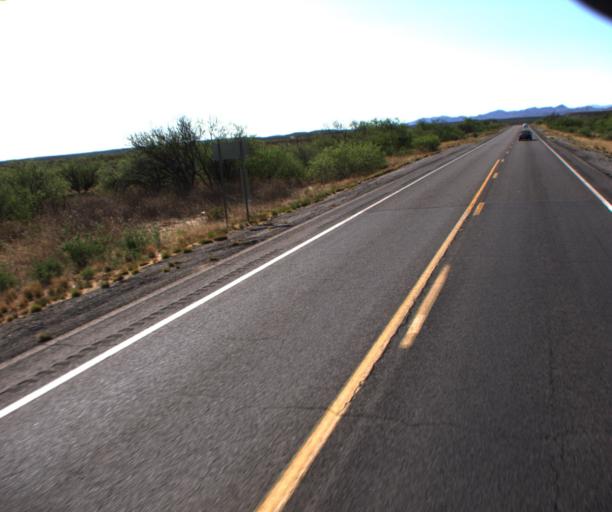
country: US
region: Arizona
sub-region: Cochise County
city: Saint David
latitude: 31.7987
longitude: -110.1565
